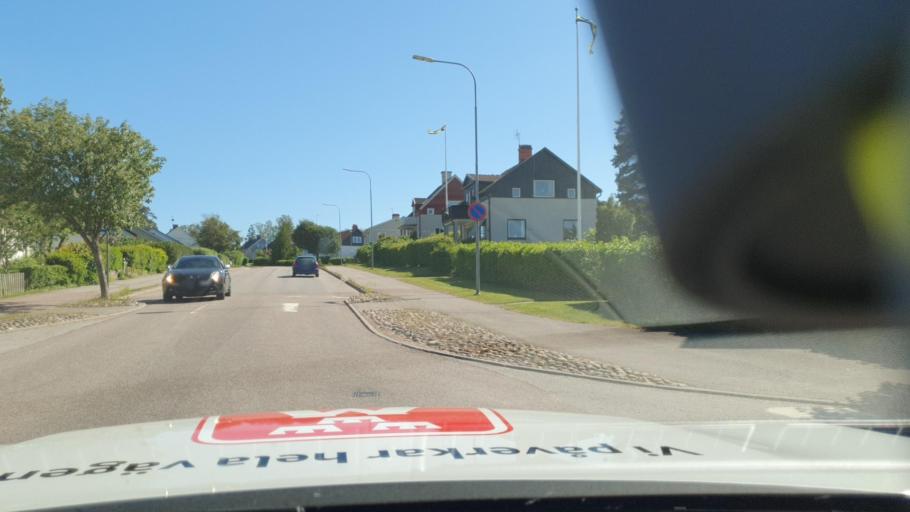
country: SE
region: Vaermland
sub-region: Kristinehamns Kommun
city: Kristinehamn
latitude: 59.3051
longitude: 14.0894
